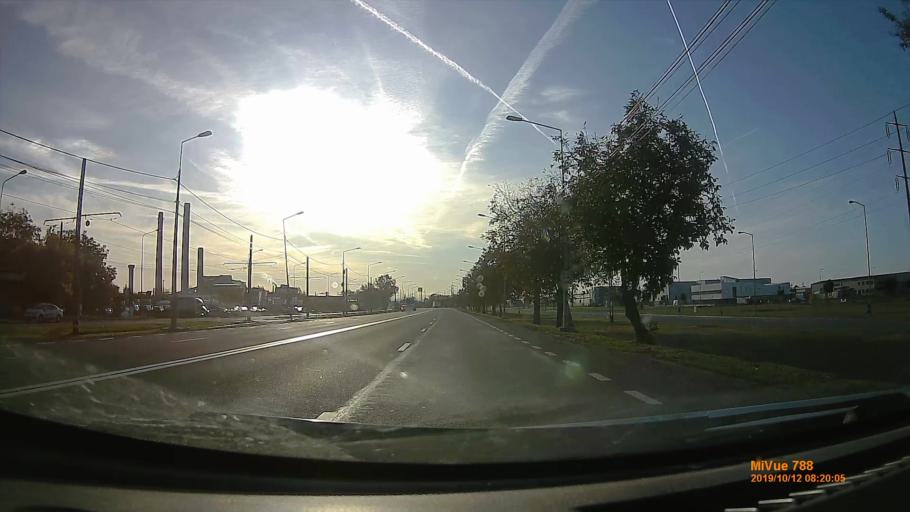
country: RO
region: Bihor
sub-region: Comuna Santandrei
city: Santandrei
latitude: 47.0871
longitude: 21.8794
